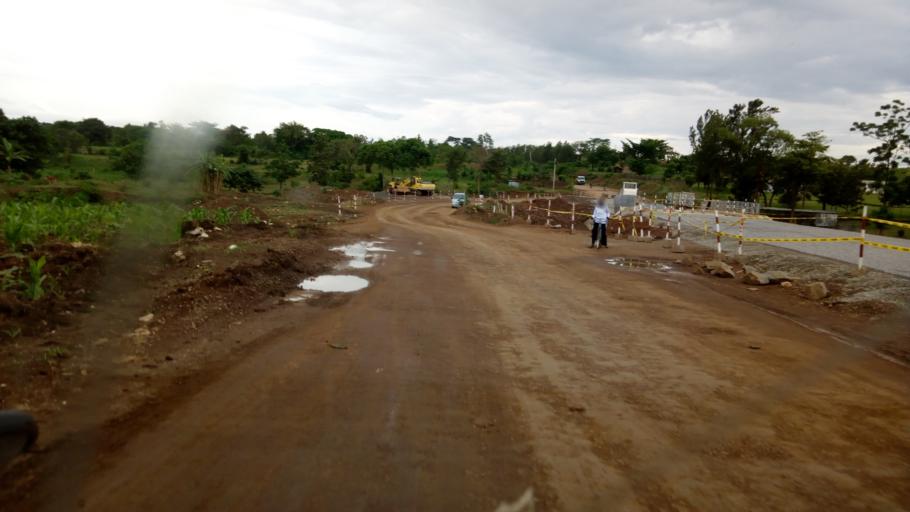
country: UG
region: Eastern Region
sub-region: Mbale District
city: Mbale
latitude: 0.9377
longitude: 34.1582
